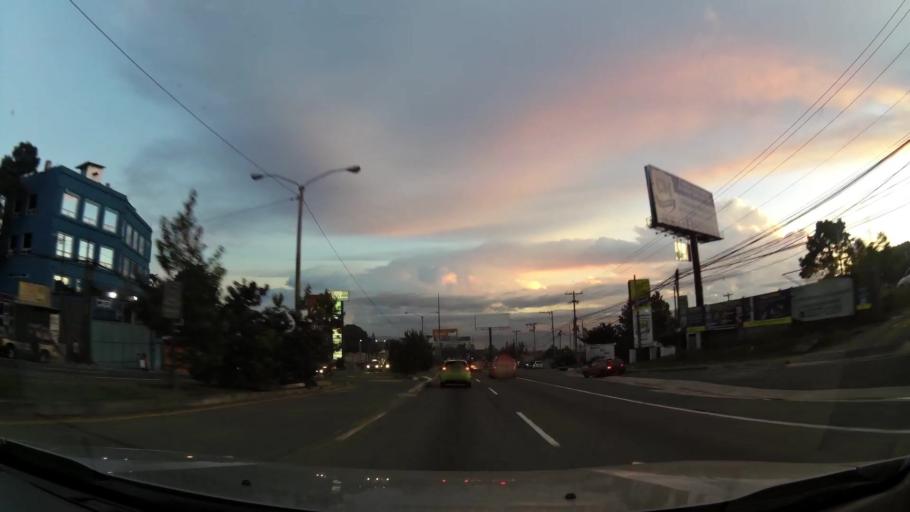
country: GT
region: Guatemala
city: Mixco
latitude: 14.6185
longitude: -90.6113
